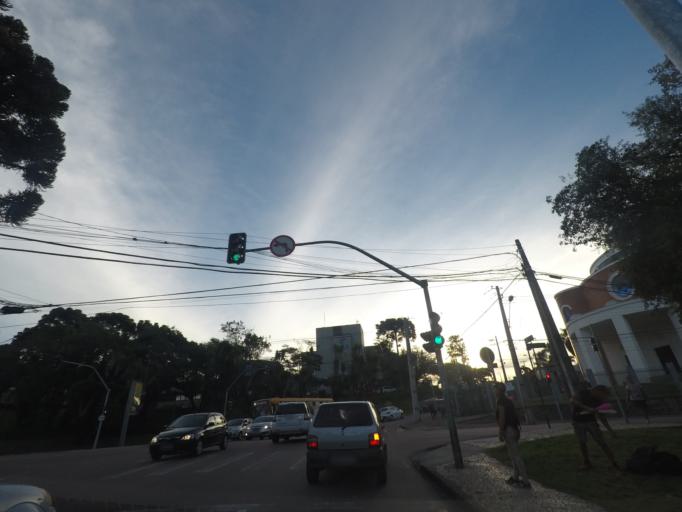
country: BR
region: Parana
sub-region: Curitiba
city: Curitiba
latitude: -25.4115
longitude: -49.2716
